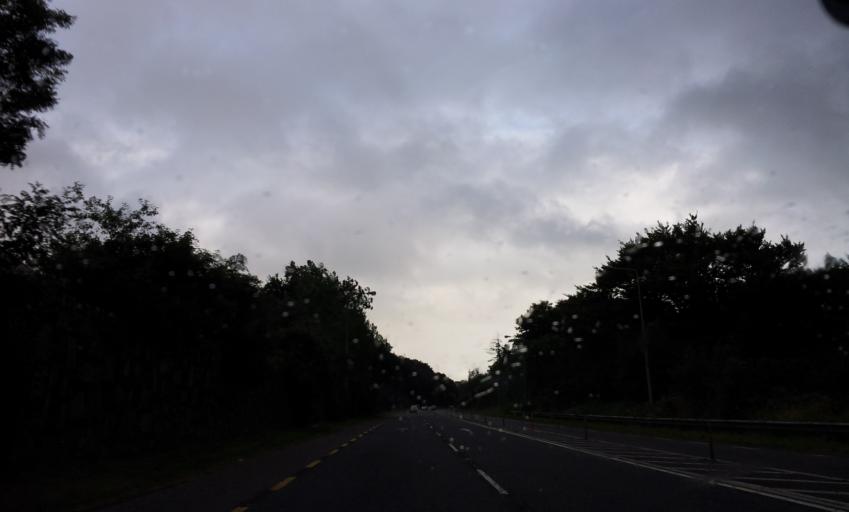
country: IE
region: Munster
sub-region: County Cork
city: Cork
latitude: 51.8740
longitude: -8.4120
